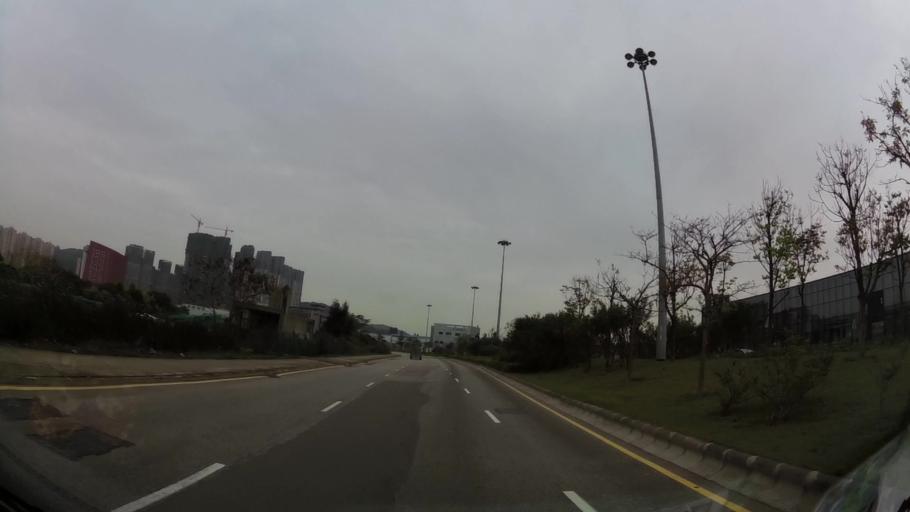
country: MO
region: Macau
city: Macau
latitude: 22.1348
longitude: 113.5526
